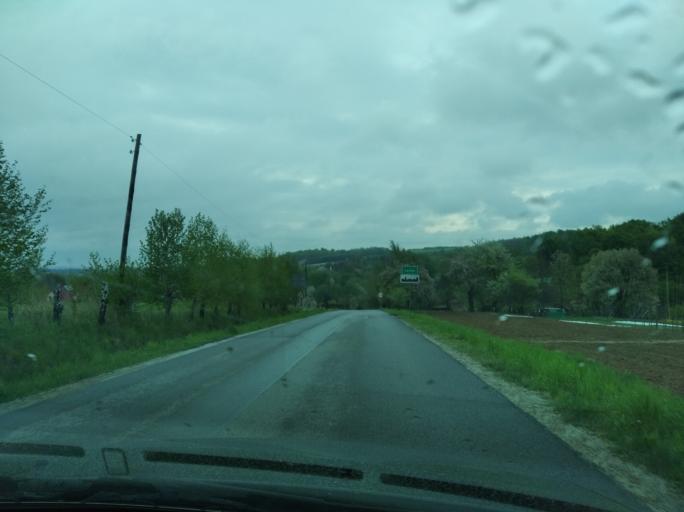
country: PL
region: Subcarpathian Voivodeship
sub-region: Powiat rzeszowski
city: Lecka
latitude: 49.8751
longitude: 21.9909
